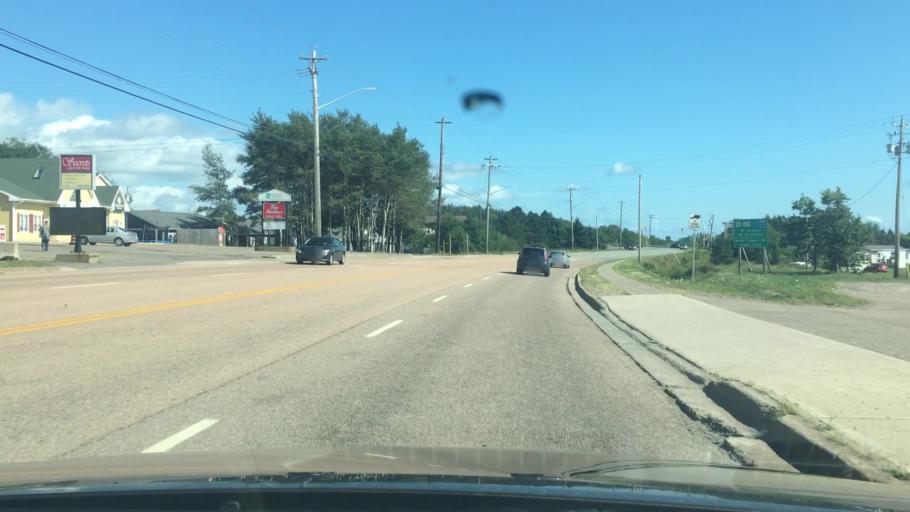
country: CA
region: Nova Scotia
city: Port Hawkesbury
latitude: 45.6135
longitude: -61.3480
